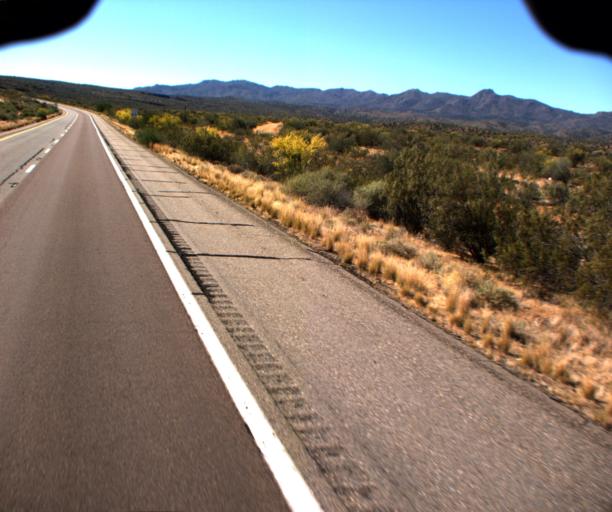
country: US
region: Arizona
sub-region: Yavapai County
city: Bagdad
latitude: 34.5114
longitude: -113.4166
